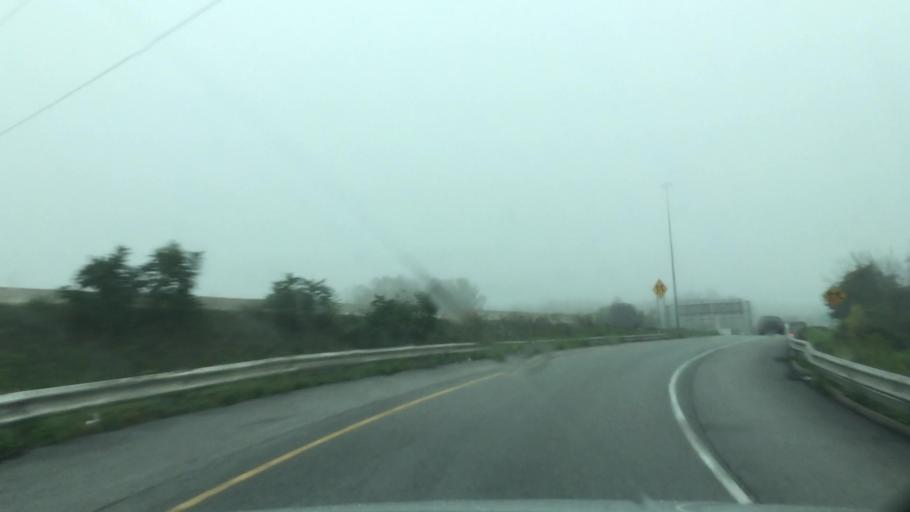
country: US
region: Indiana
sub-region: Lake County
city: Lake Station
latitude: 41.5924
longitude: -87.2344
